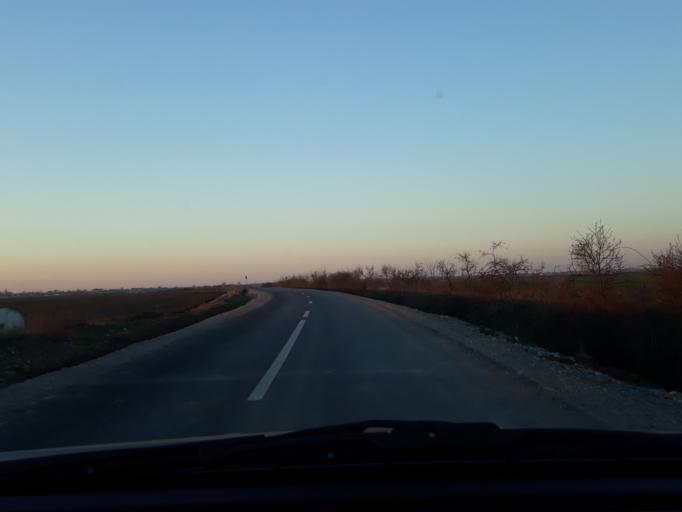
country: RO
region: Bihor
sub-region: Comuna Gepiu
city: Gepiu
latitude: 46.9117
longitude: 21.7879
